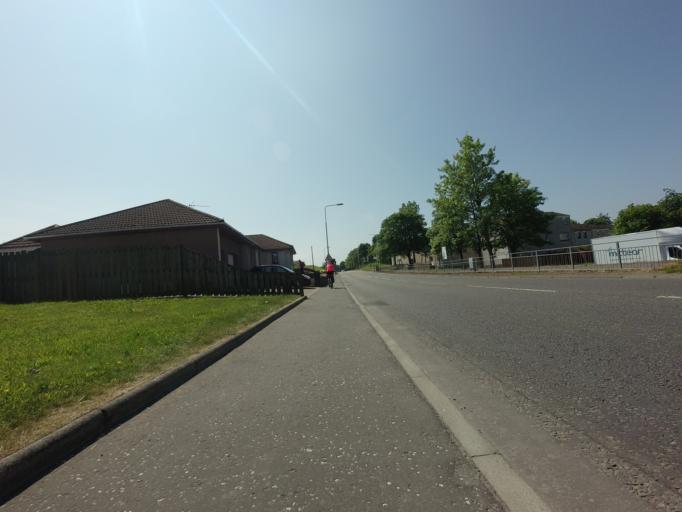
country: GB
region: Scotland
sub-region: Fife
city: Townhill
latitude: 56.0627
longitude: -3.4143
